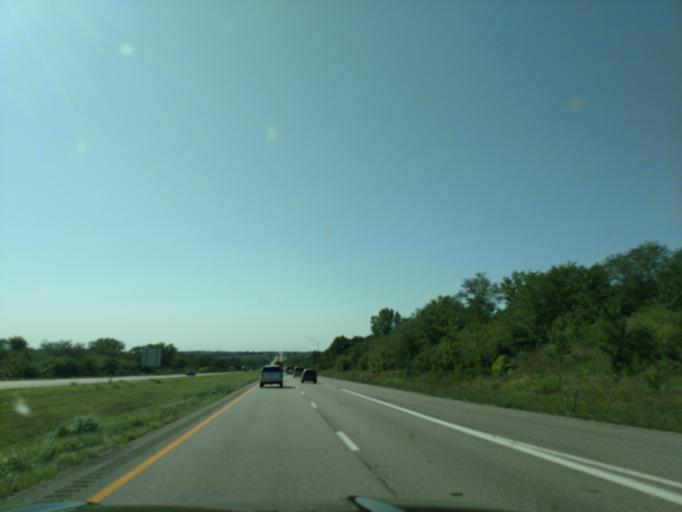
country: US
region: Missouri
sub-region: Andrew County
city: Country Club Village
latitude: 39.8602
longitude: -94.8139
